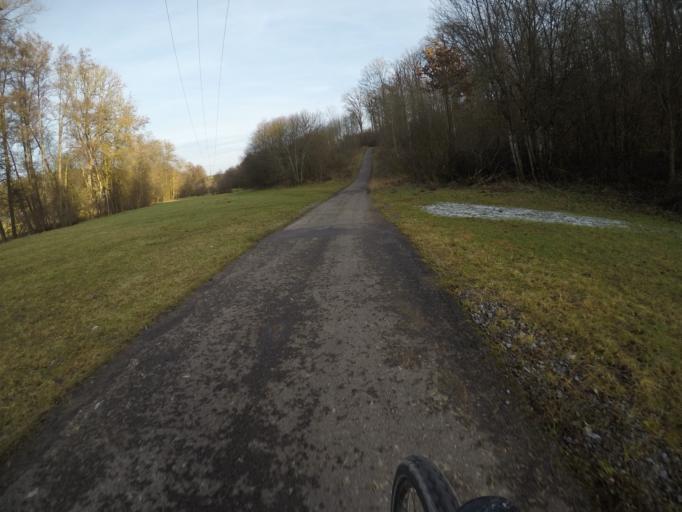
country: DE
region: Baden-Wuerttemberg
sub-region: Regierungsbezirk Stuttgart
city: Schonaich
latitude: 48.6505
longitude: 9.0834
